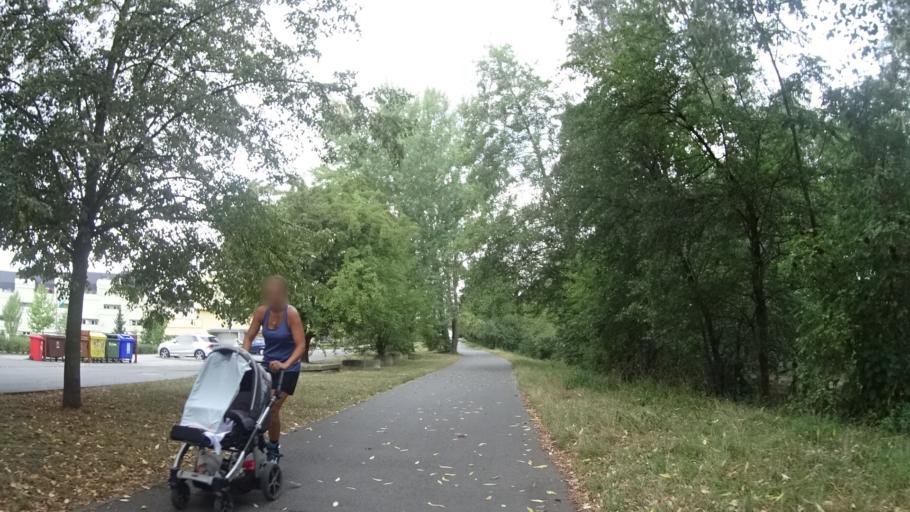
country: CZ
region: Olomoucky
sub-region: Okres Olomouc
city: Olomouc
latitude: 49.6079
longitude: 17.2402
